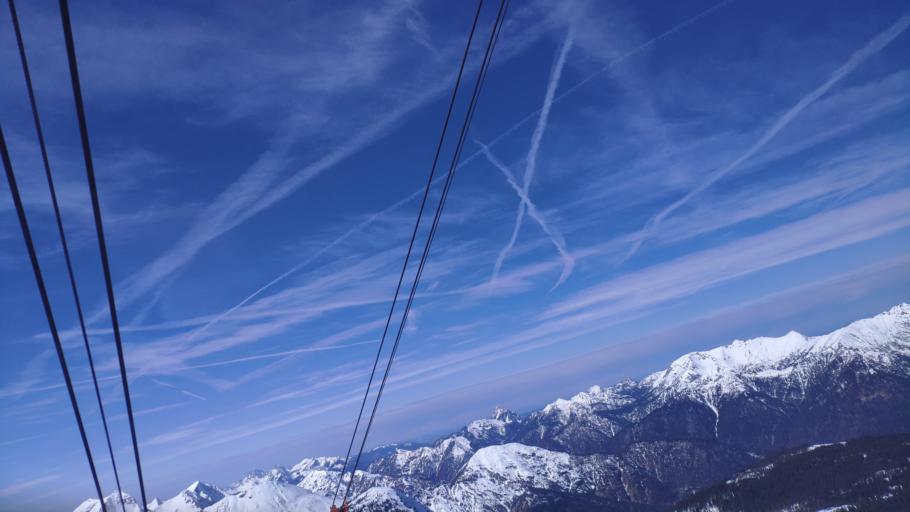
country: AT
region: Tyrol
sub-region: Politischer Bezirk Reutte
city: Ehrwald
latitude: 47.4235
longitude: 10.9683
